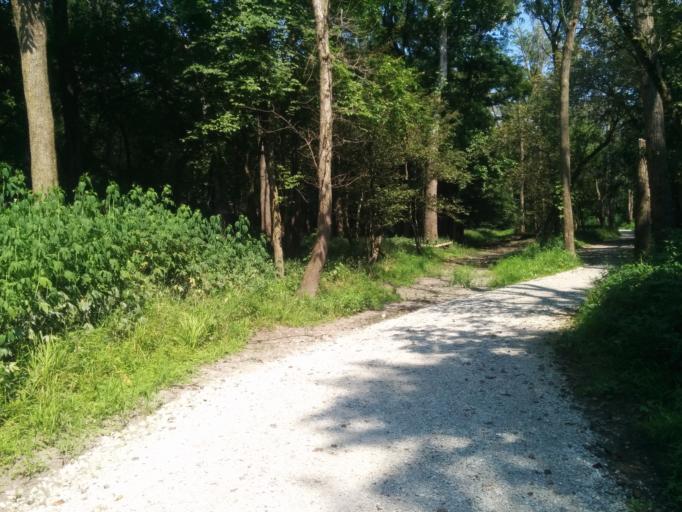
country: US
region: Illinois
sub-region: Cook County
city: River Grove
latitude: 41.9135
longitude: -87.8327
